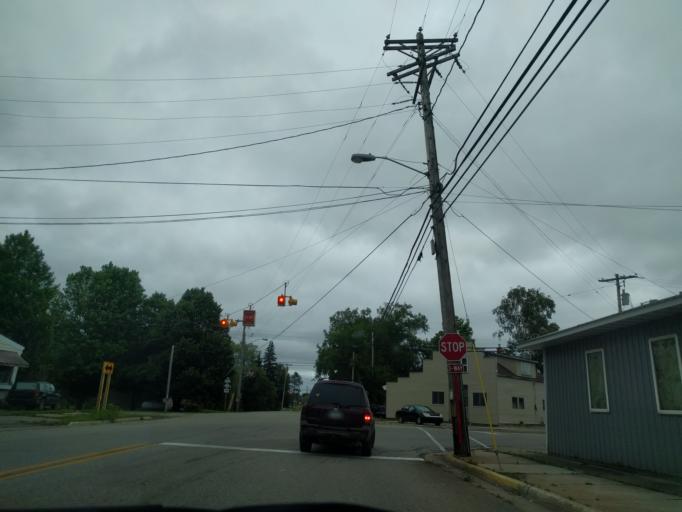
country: US
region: Michigan
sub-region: Delta County
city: Gladstone
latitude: 45.9781
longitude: -87.0715
